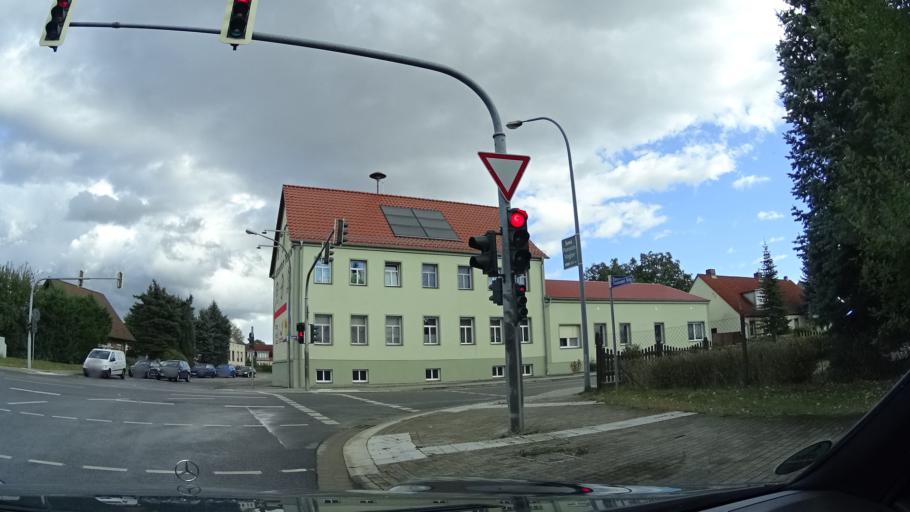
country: DE
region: Brandenburg
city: Neuruppin
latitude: 52.8930
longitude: 12.7977
